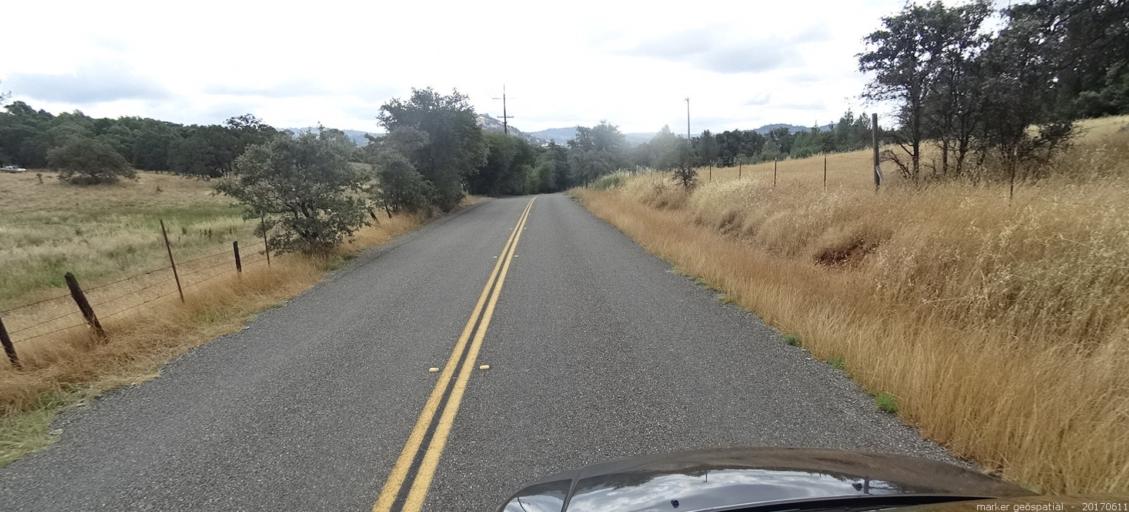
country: US
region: California
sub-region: Yuba County
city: Loma Rica
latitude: 39.3804
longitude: -121.3914
